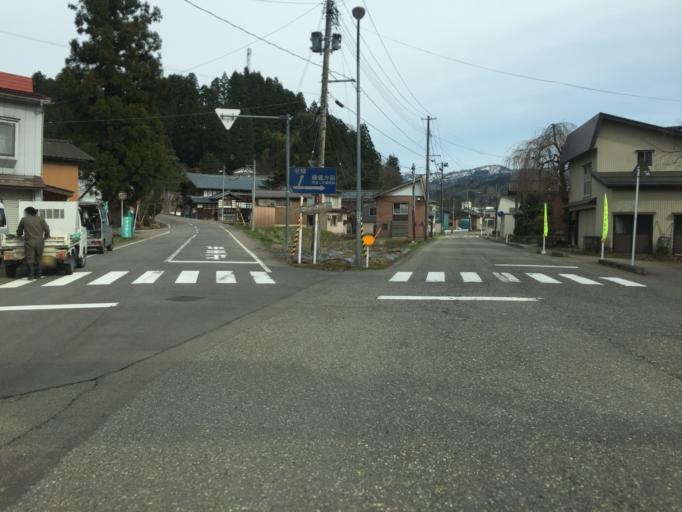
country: JP
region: Niigata
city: Tochio-honcho
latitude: 37.4509
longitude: 139.0136
